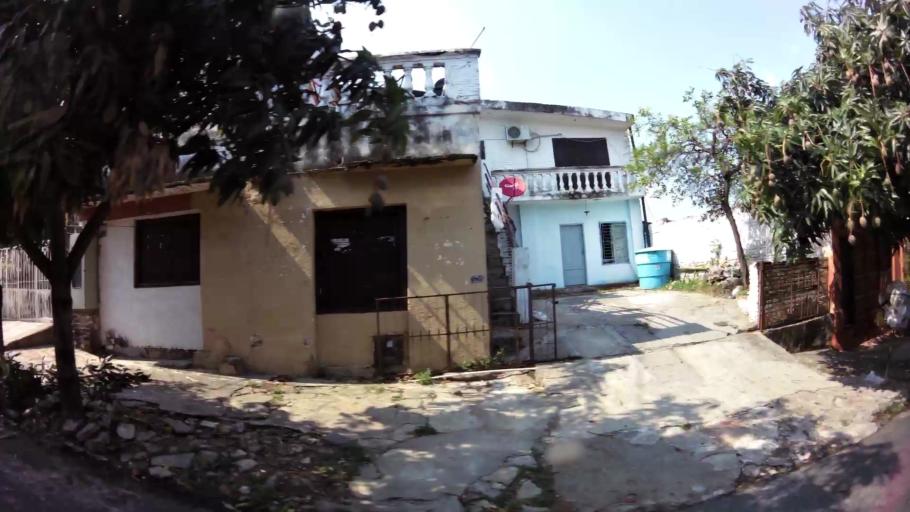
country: PY
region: Presidente Hayes
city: Nanawa
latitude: -25.2862
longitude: -57.6625
